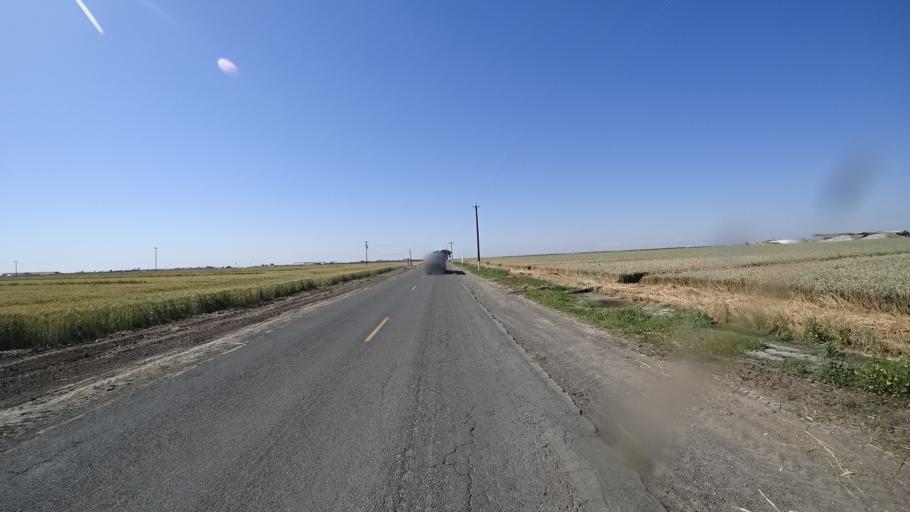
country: US
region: California
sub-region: Kings County
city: Home Garden
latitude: 36.2234
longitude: -119.5472
